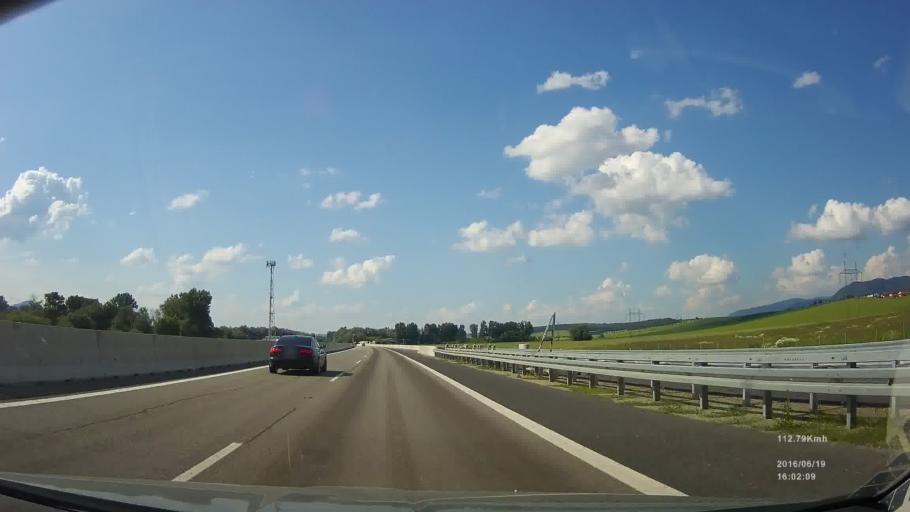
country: SK
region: Kosicky
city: Kosice
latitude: 48.8322
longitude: 21.3066
